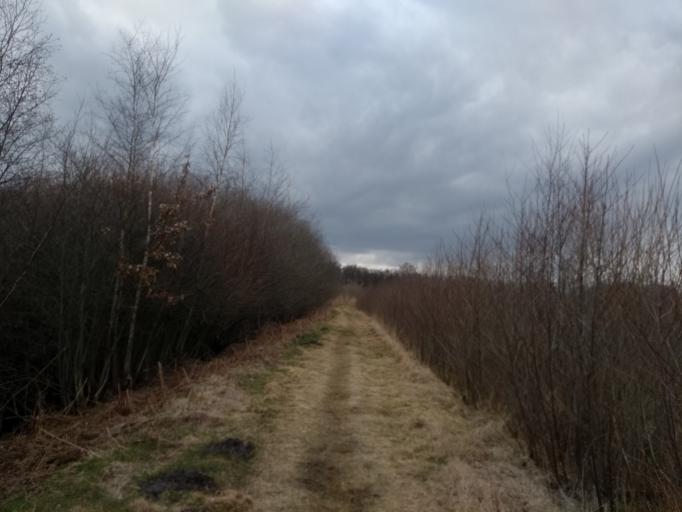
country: NL
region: Overijssel
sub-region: Gemeente Haaksbergen
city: Haaksbergen
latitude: 52.1209
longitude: 6.7731
